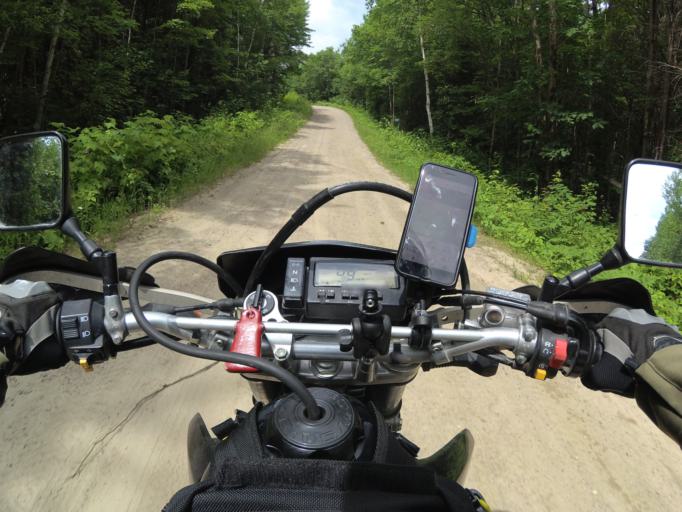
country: CA
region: Ontario
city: Bancroft
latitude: 44.8282
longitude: -77.3099
